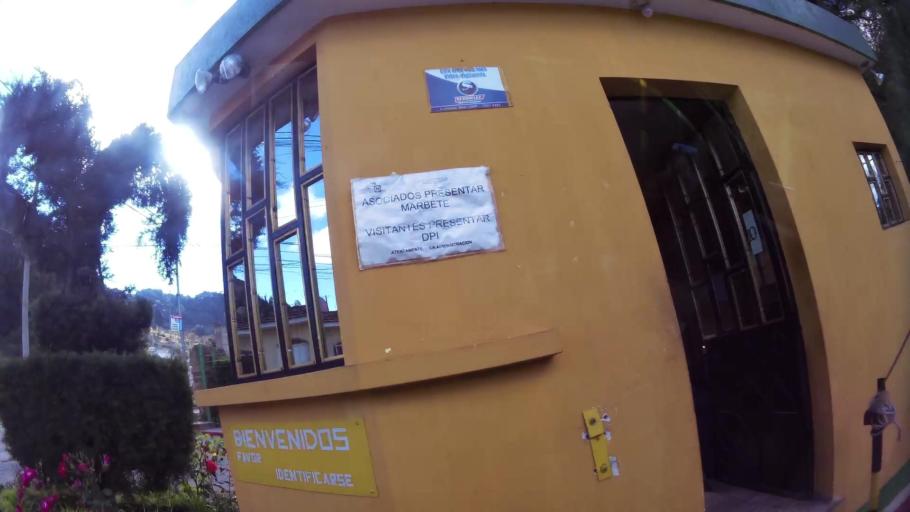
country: GT
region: Quetzaltenango
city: Quetzaltenango
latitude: 14.8304
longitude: -91.5094
